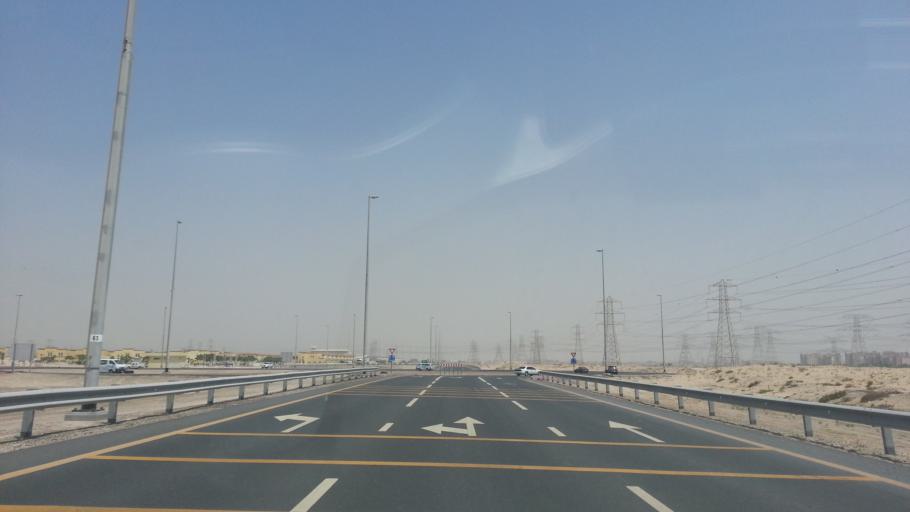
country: AE
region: Dubai
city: Dubai
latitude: 25.0412
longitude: 55.1551
